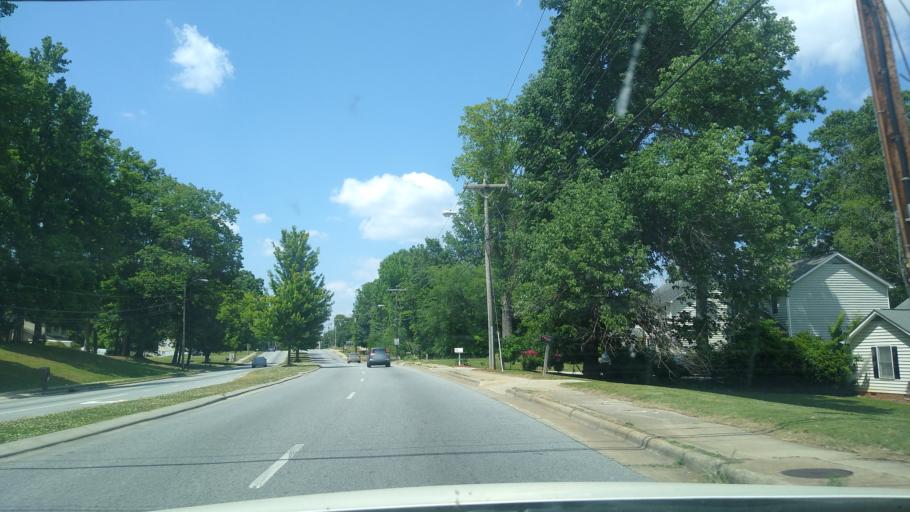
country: US
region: North Carolina
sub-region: Guilford County
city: Greensboro
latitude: 36.0211
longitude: -79.7918
